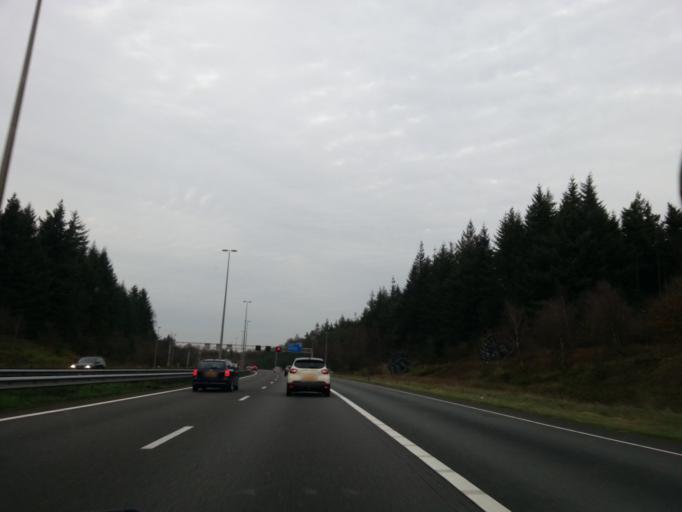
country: NL
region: Gelderland
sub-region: Gemeente Apeldoorn
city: Beekbergen
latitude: 52.1065
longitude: 5.9548
